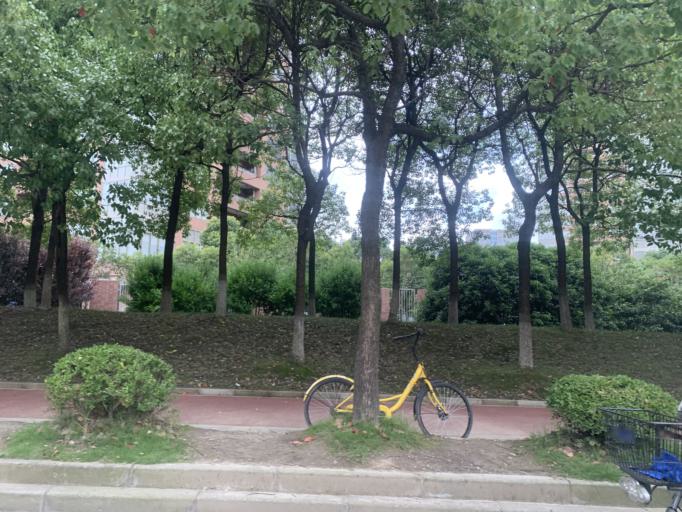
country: CN
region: Shanghai Shi
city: Huamu
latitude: 31.2169
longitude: 121.5353
